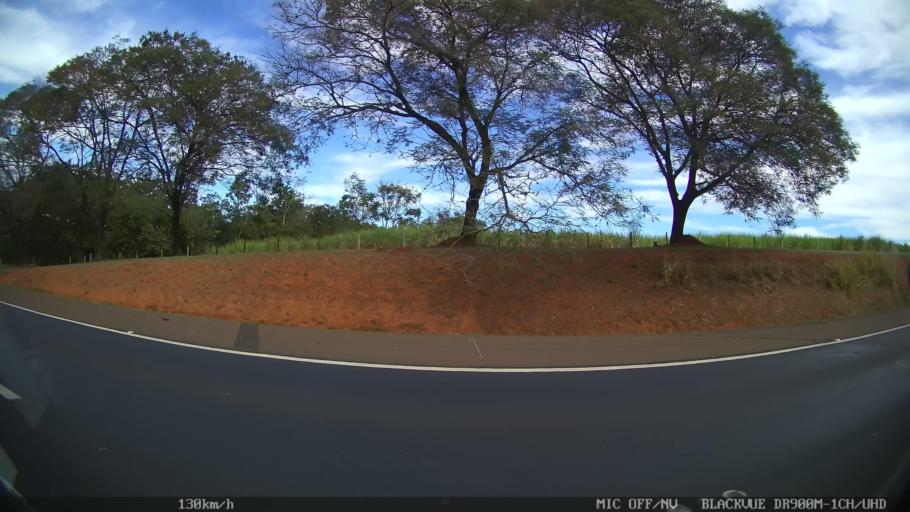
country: BR
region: Sao Paulo
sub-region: Taquaritinga
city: Taquaritinga
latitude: -21.4928
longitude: -48.5740
